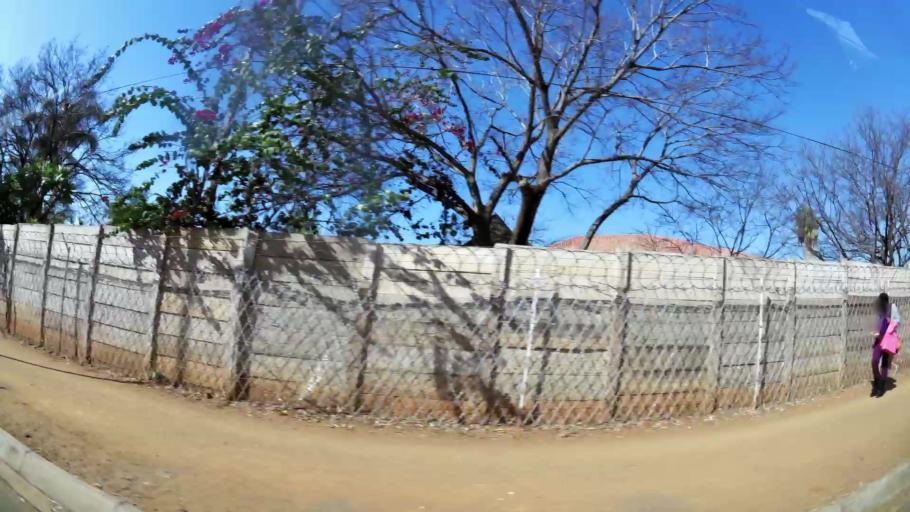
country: ZA
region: Gauteng
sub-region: City of Tshwane Metropolitan Municipality
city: Pretoria
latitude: -25.6761
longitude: 28.2543
